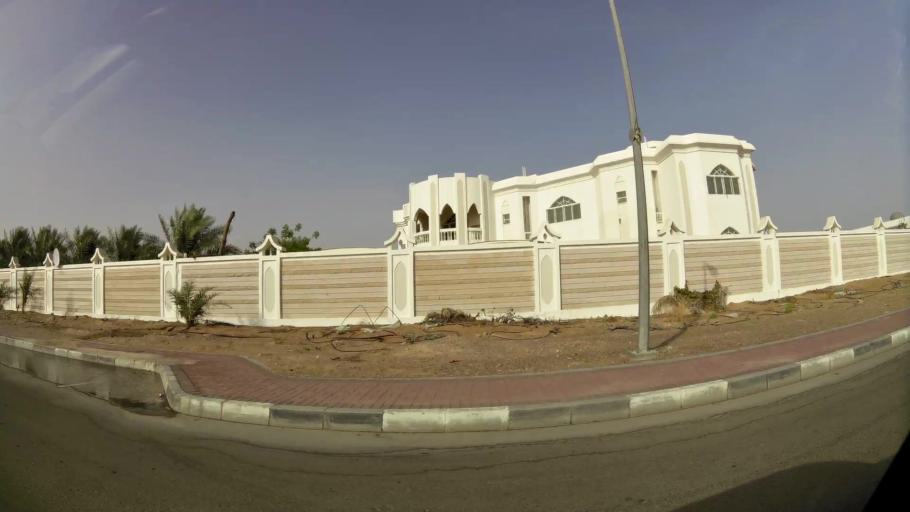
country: AE
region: Abu Dhabi
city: Al Ain
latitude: 24.2187
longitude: 55.6464
